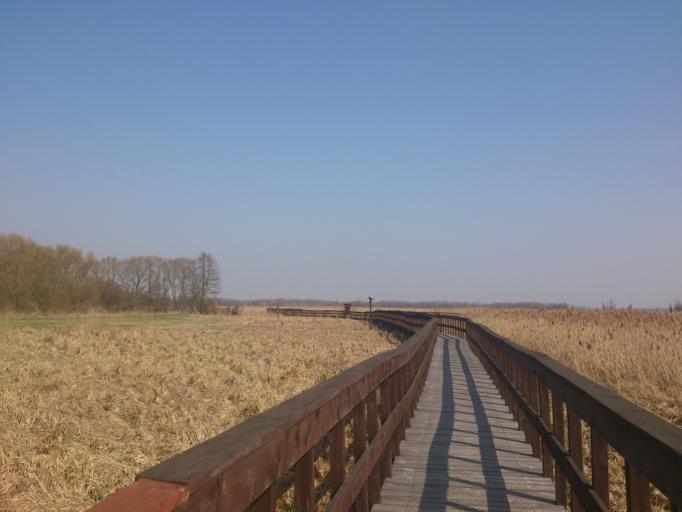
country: PL
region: Podlasie
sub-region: Powiat bialostocki
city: Tykocin
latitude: 53.1046
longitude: 22.7981
